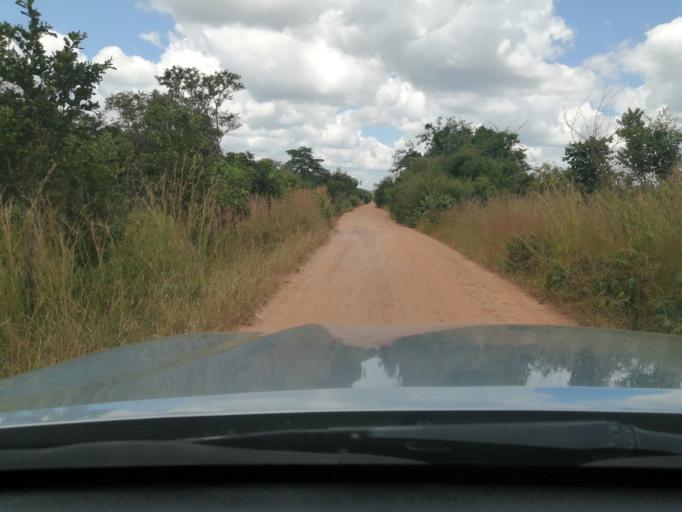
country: ZM
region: Lusaka
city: Lusaka
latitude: -15.1562
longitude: 27.9510
